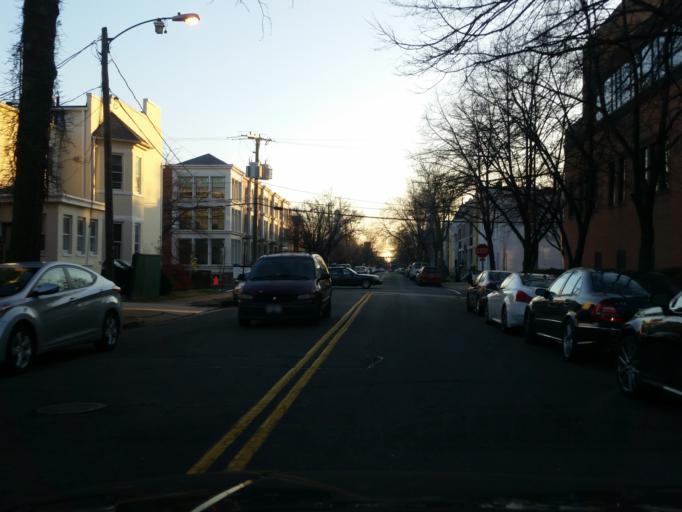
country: US
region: Virginia
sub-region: City of Alexandria
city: Alexandria
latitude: 38.8091
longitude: -77.0473
